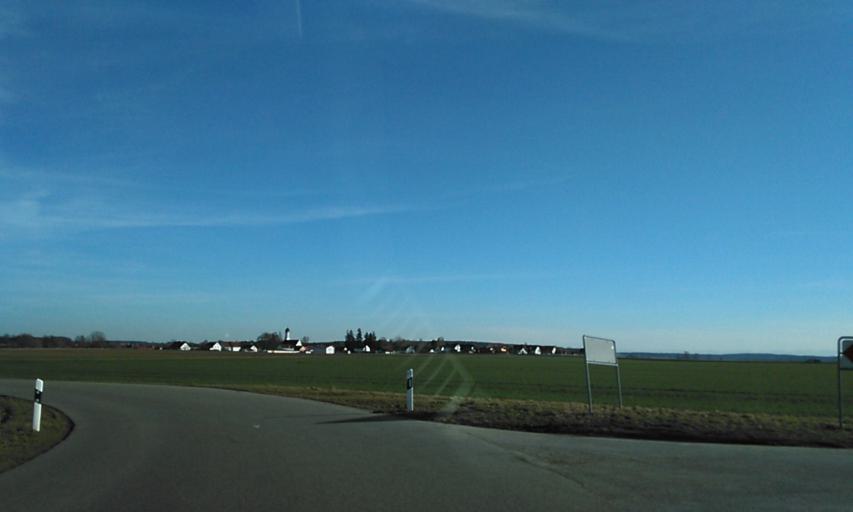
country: DE
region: Bavaria
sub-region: Swabia
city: Steindorf
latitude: 48.2233
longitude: 10.9937
